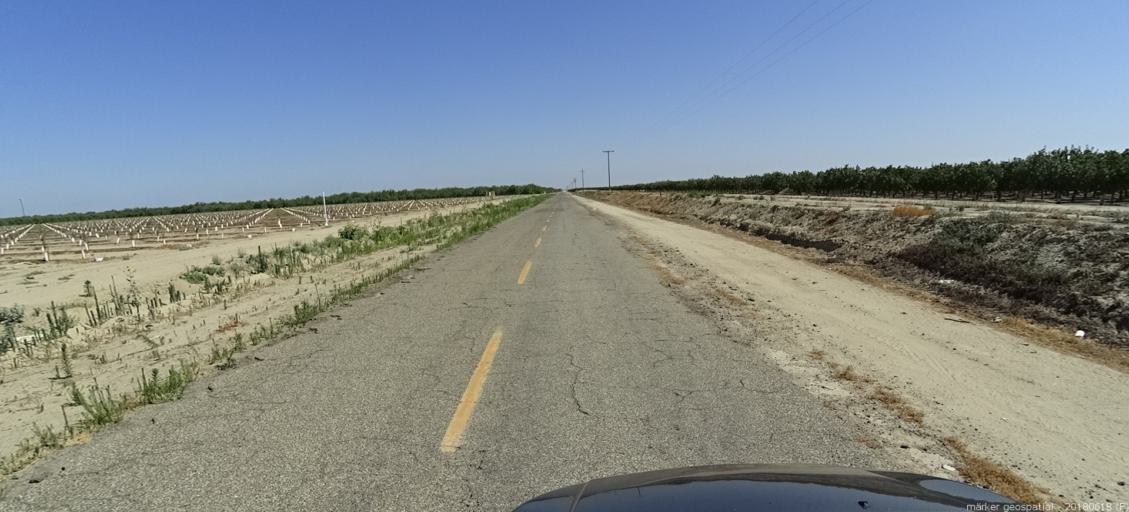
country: US
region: California
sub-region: Fresno County
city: Mendota
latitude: 36.8396
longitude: -120.2552
